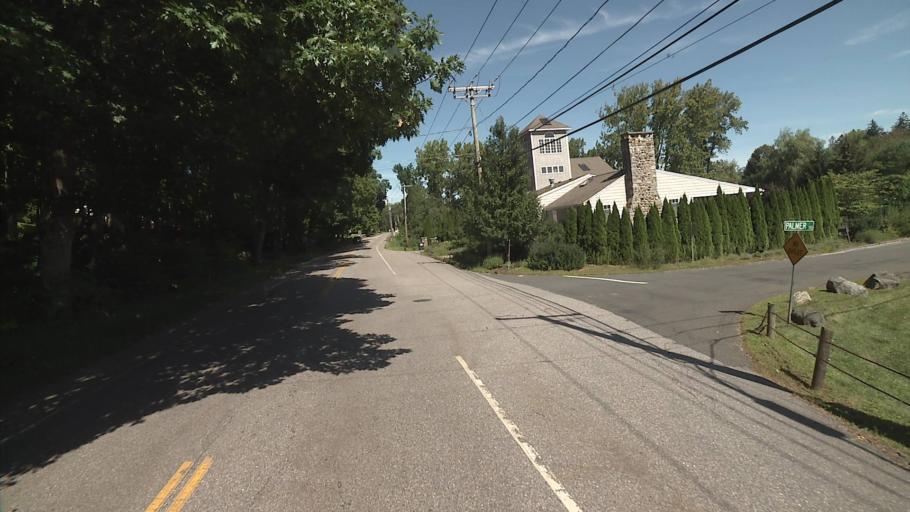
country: US
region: Connecticut
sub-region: Litchfield County
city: Bethlehem Village
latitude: 41.6940
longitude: -73.2323
